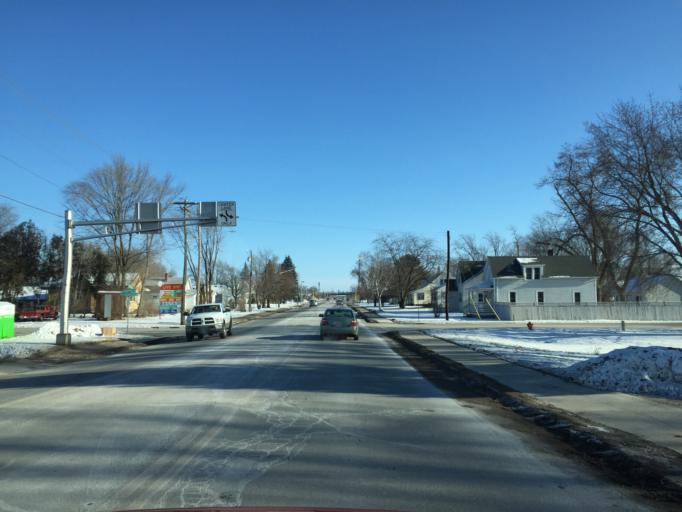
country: US
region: Minnesota
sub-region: Isanti County
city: Cambridge
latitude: 45.5727
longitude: -93.2196
